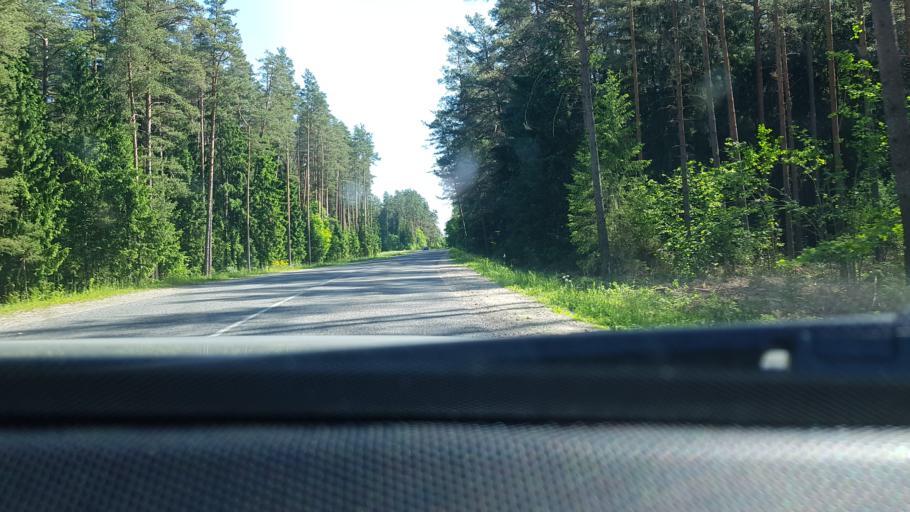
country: LV
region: Kraslavas Rajons
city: Kraslava
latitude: 55.8880
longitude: 27.1451
